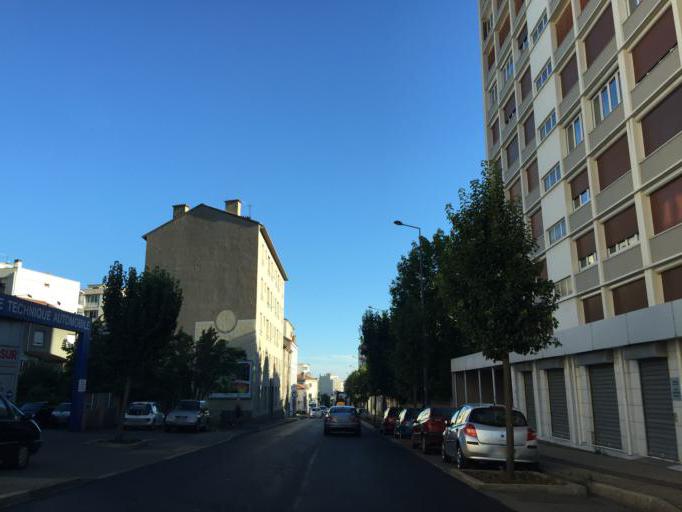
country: FR
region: Rhone-Alpes
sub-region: Departement de la Loire
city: Saint-Etienne
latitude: 45.4123
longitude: 4.3972
